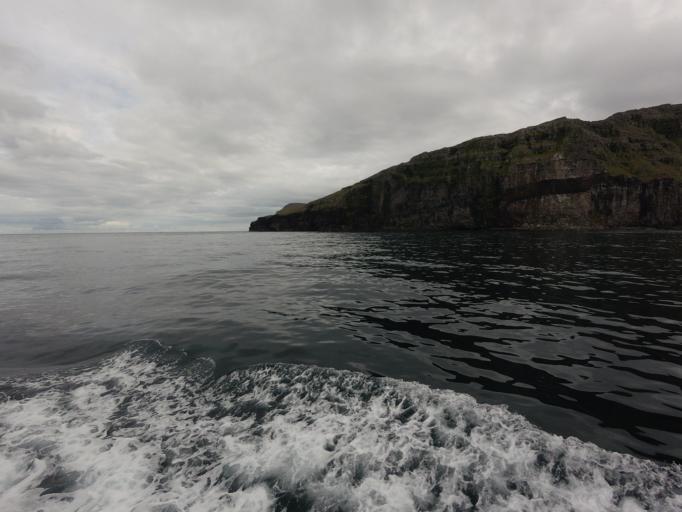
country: FO
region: Nordoyar
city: Klaksvik
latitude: 62.3098
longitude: -6.3456
